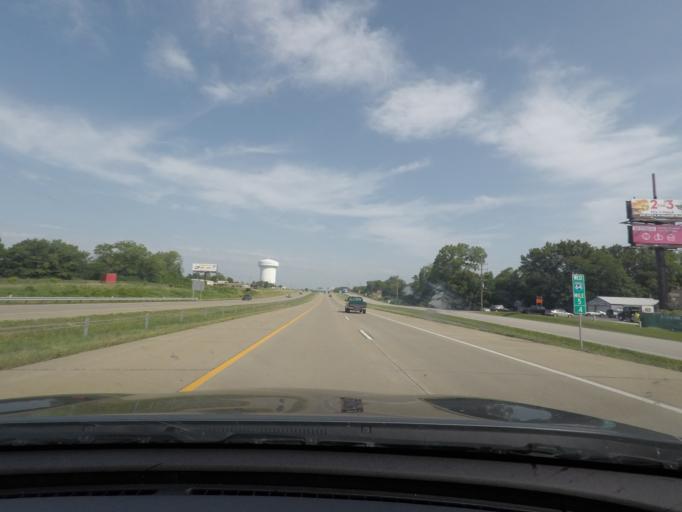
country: US
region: Missouri
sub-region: Saint Charles County
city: Dardenne Prairie
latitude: 38.7577
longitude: -90.7615
